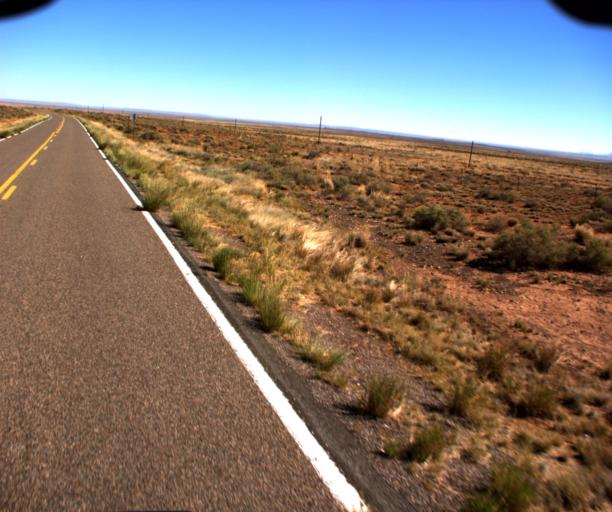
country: US
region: Arizona
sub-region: Coconino County
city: LeChee
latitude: 35.1033
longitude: -110.8639
